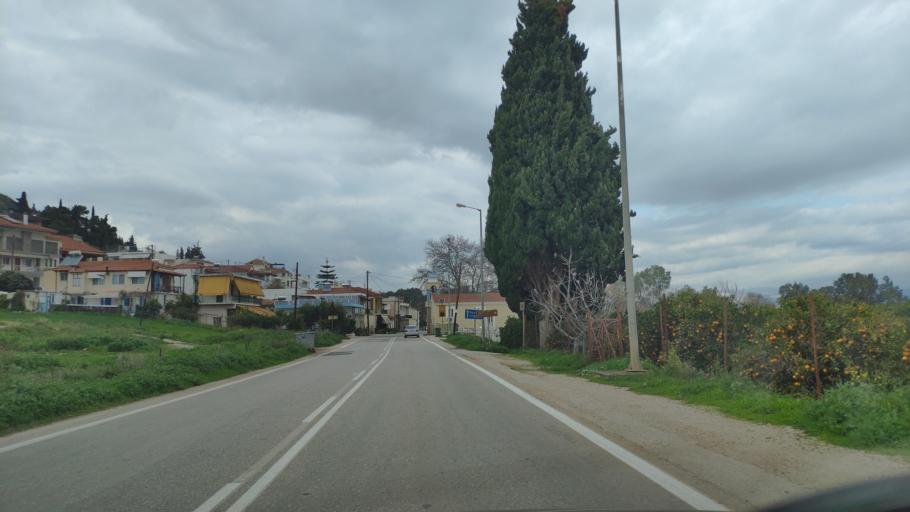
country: GR
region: Peloponnese
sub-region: Nomos Argolidos
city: Nea Kios
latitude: 37.5505
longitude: 22.7169
